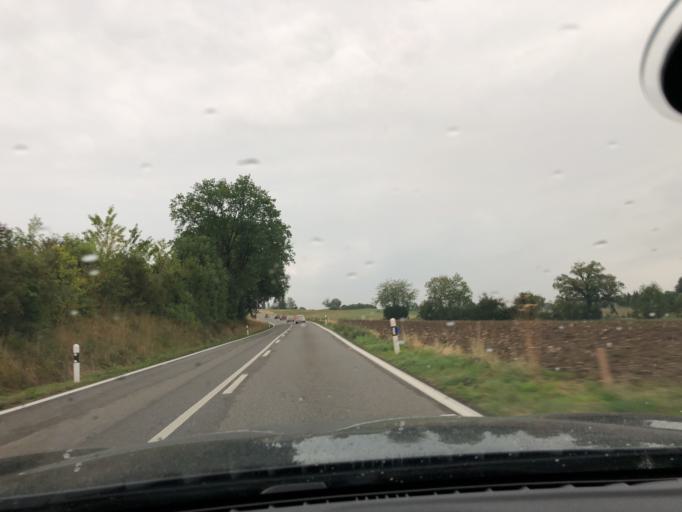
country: CH
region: Aargau
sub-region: Bezirk Bremgarten
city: Berikon
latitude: 47.3482
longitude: 8.3675
